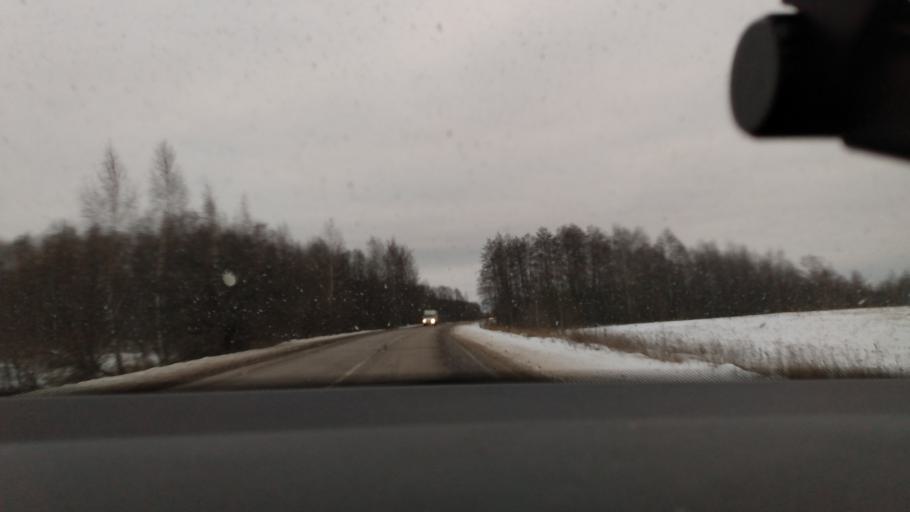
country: RU
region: Moskovskaya
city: Krasnaya Poyma
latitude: 55.1553
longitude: 39.2208
